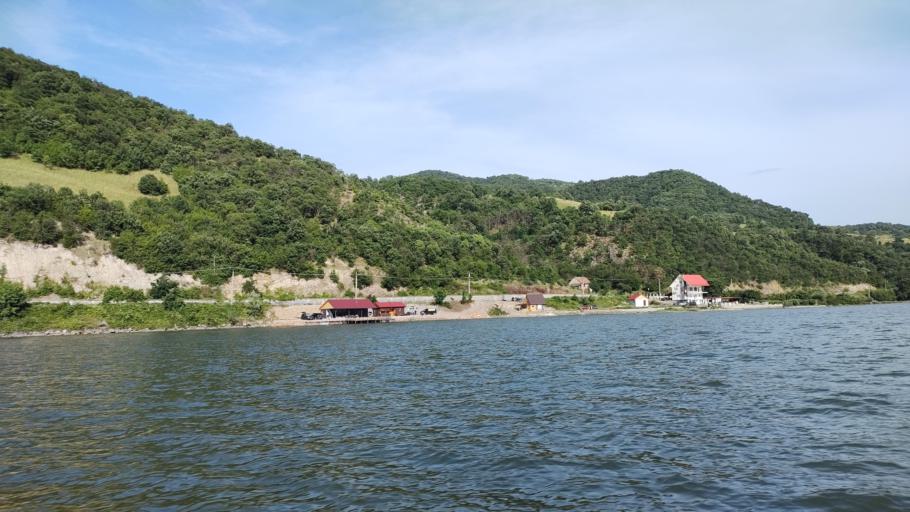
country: RO
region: Mehedinti
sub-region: Comuna Svinita
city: Svinita
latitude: 44.5615
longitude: 22.0310
